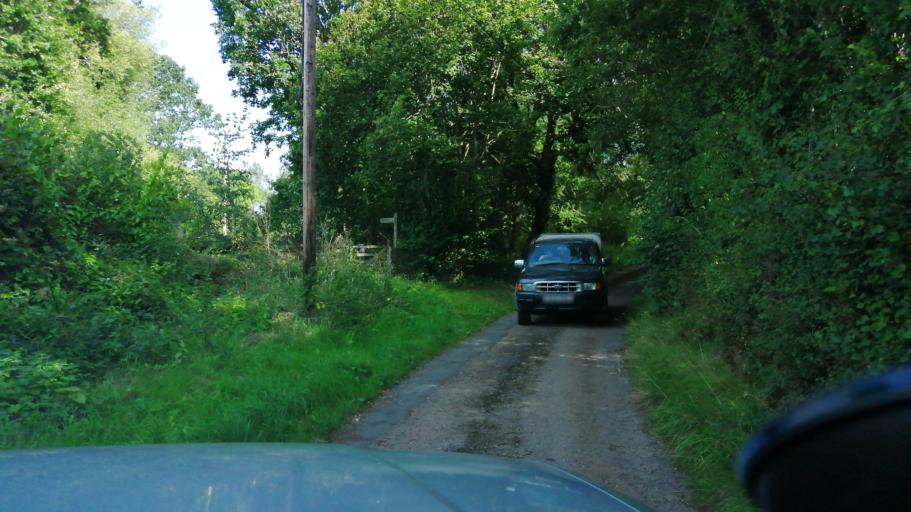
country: GB
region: England
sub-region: Herefordshire
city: Kingstone
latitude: 52.0345
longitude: -2.8188
